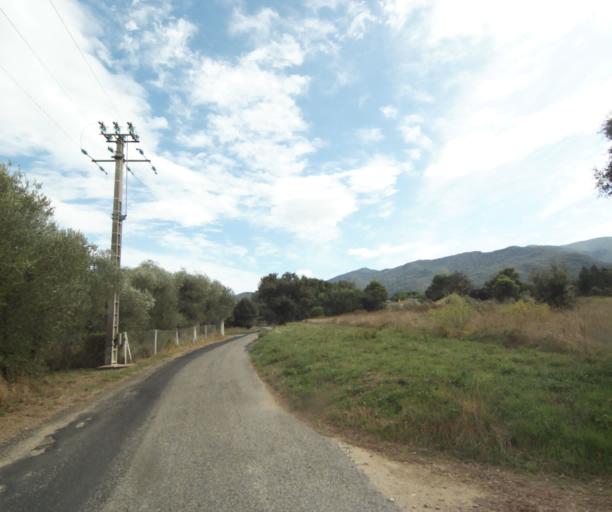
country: FR
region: Languedoc-Roussillon
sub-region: Departement des Pyrenees-Orientales
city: Argelers
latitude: 42.5463
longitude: 2.9984
